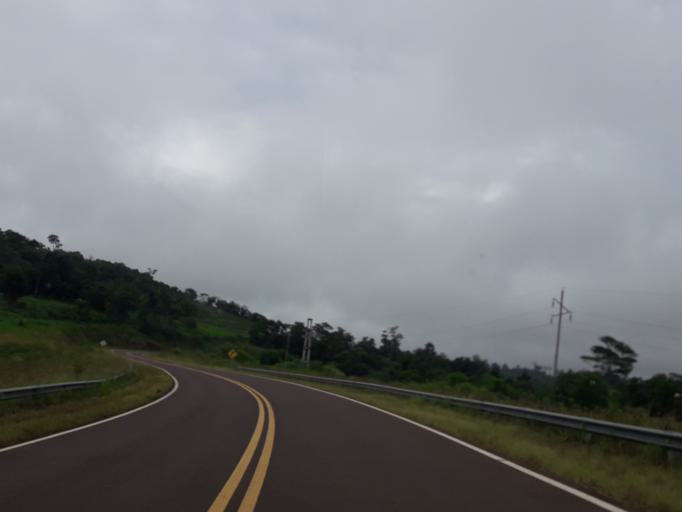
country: AR
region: Misiones
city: Bernardo de Irigoyen
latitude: -26.3934
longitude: -53.8071
